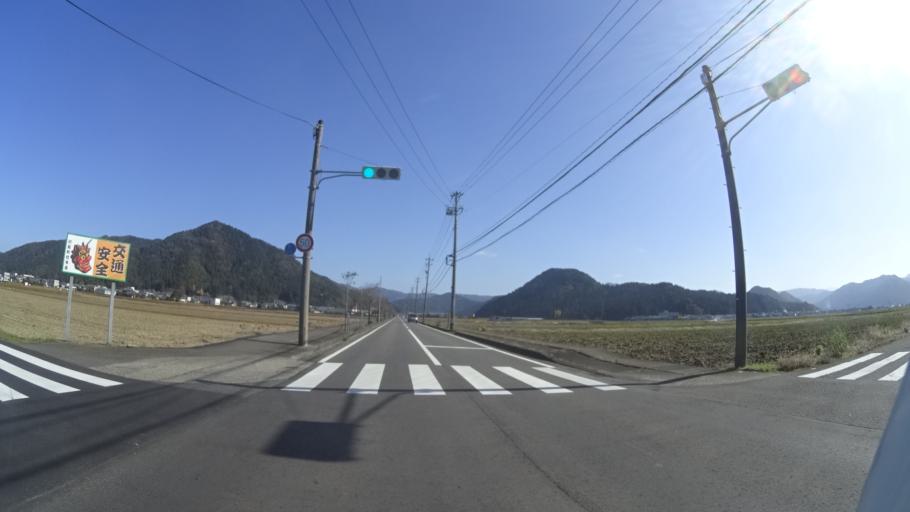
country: JP
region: Fukui
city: Sabae
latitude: 35.9483
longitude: 136.2366
